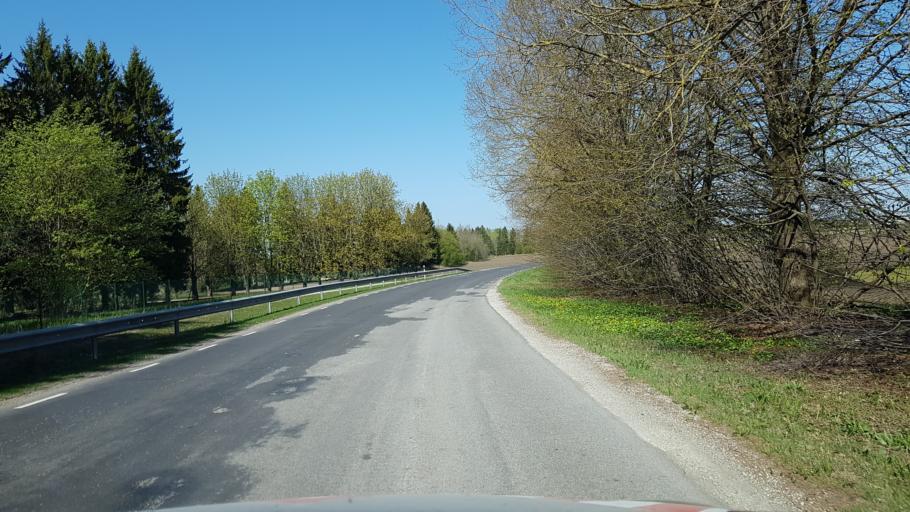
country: EE
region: Harju
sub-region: Joelaehtme vald
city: Loo
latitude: 59.4178
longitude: 24.9433
